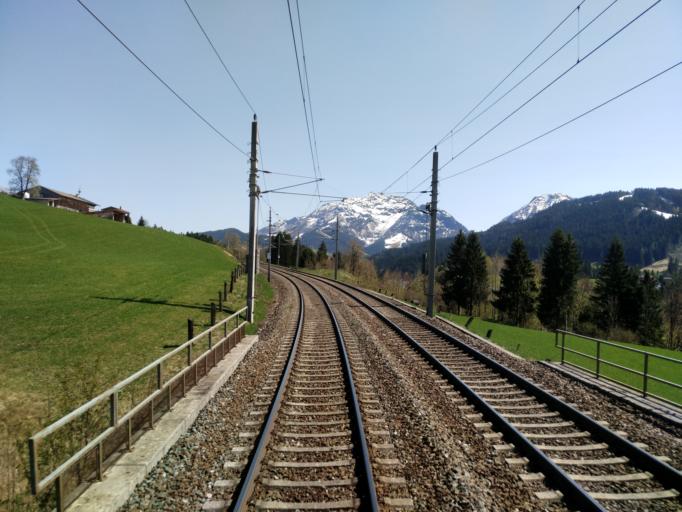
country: AT
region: Tyrol
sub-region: Politischer Bezirk Kitzbuhel
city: Fieberbrunn
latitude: 47.4761
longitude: 12.5509
